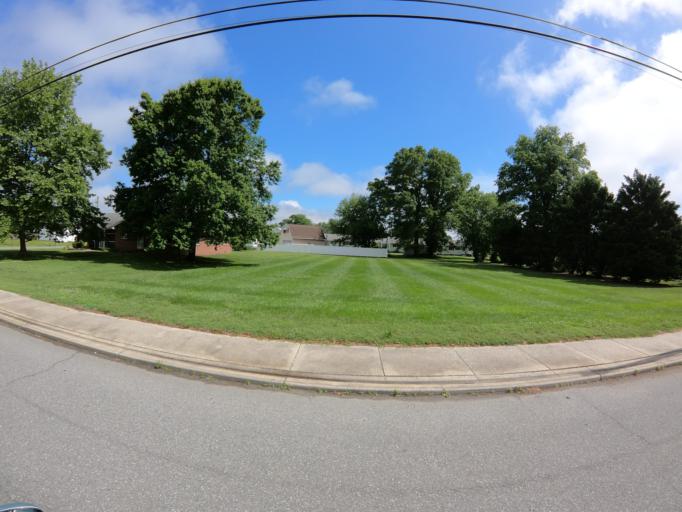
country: US
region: Delaware
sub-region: Kent County
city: Felton
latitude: 39.0077
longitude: -75.5728
